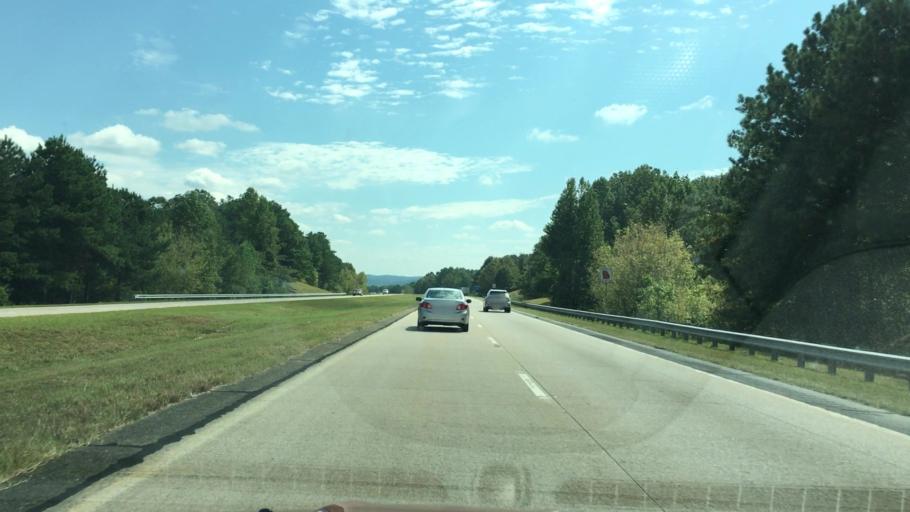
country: US
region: Georgia
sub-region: Pickens County
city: Jasper
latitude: 34.5473
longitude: -84.5202
